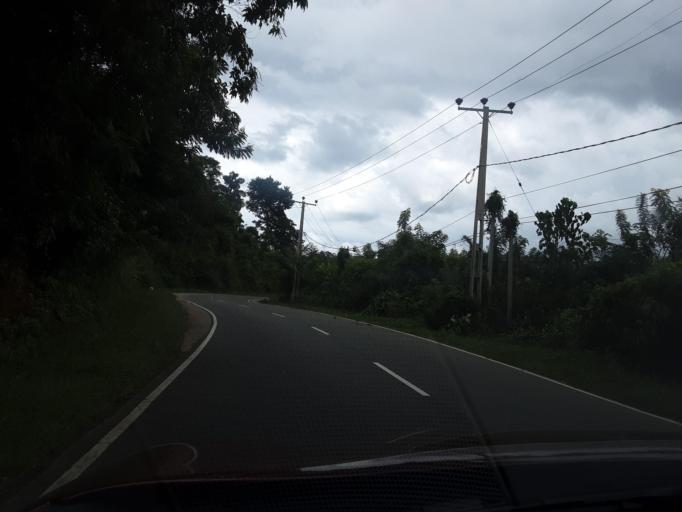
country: LK
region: Uva
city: Monaragala
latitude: 6.9091
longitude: 81.2111
